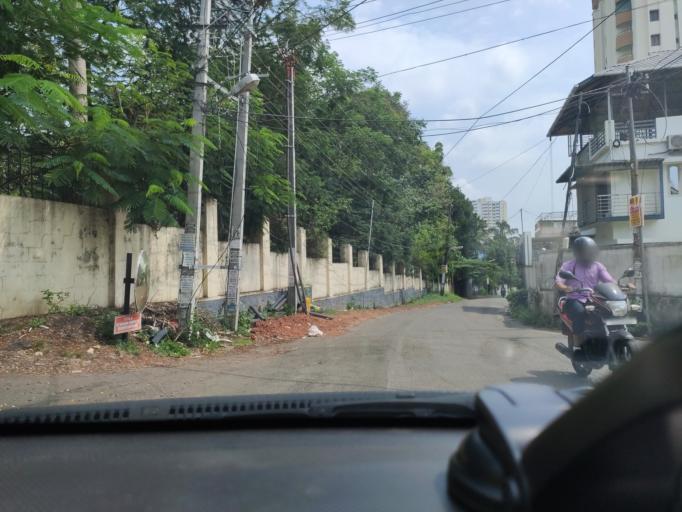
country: IN
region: Kerala
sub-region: Ernakulam
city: Elur
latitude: 10.0287
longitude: 76.3292
